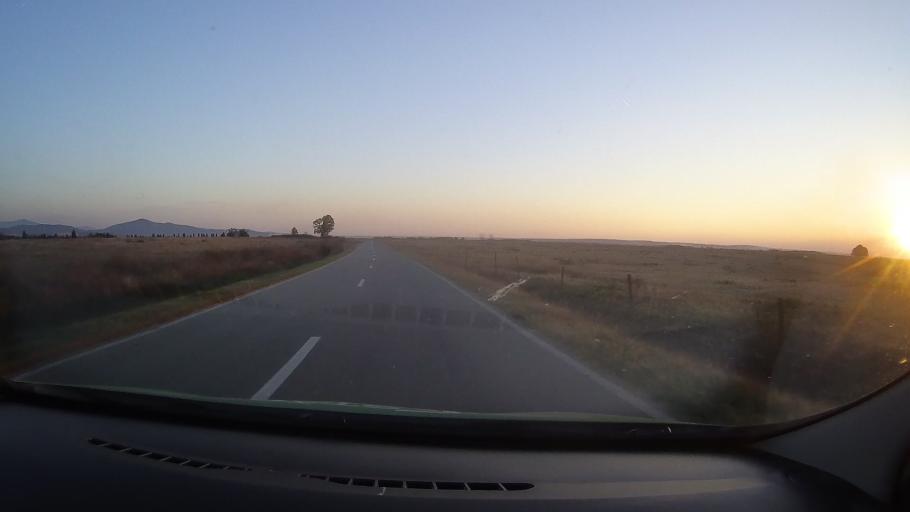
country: RO
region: Timis
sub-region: Comuna Manastiur
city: Manastiur
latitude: 45.8227
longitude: 22.0709
